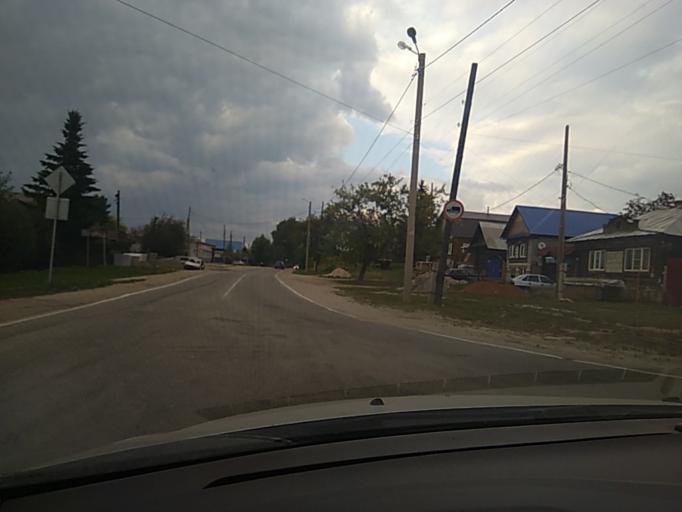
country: RU
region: Chelyabinsk
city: Kyshtym
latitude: 55.6956
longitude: 60.5520
